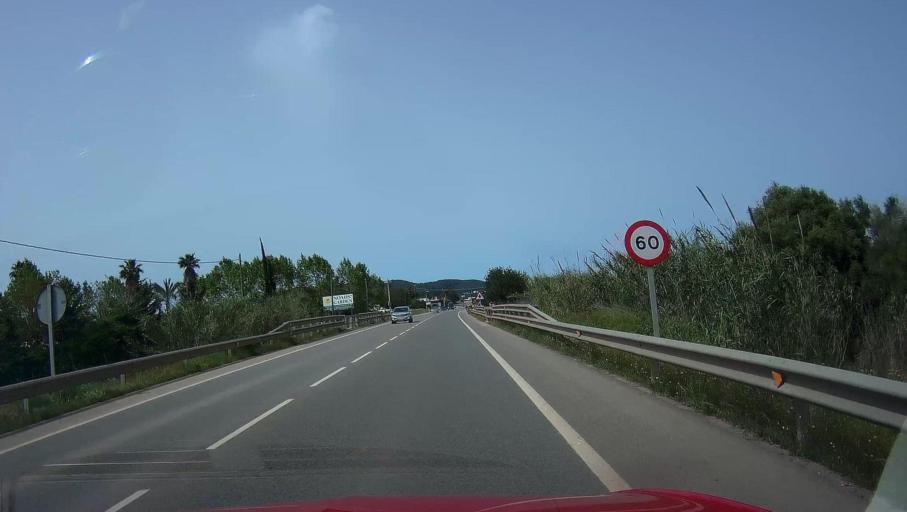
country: ES
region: Balearic Islands
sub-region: Illes Balears
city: Santa Eularia des Riu
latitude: 39.0083
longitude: 1.4881
